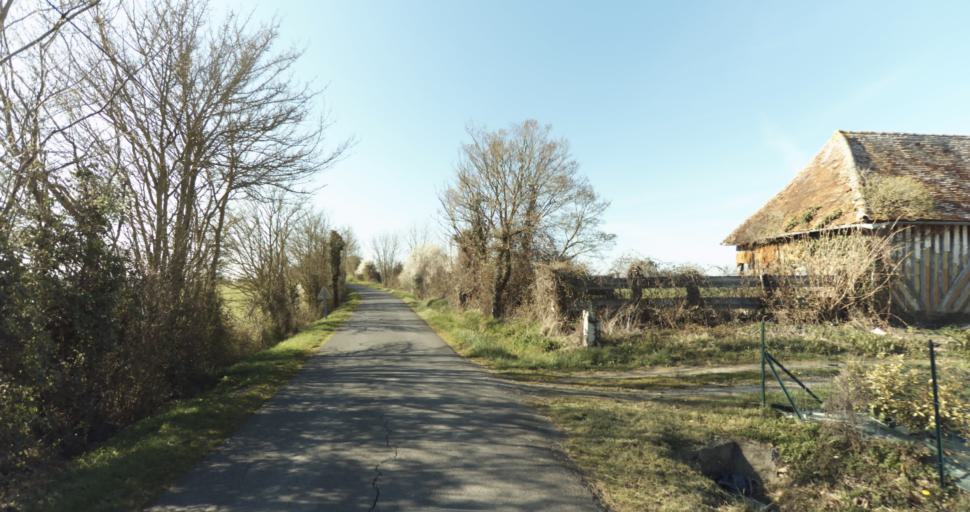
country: FR
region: Lower Normandy
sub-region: Departement du Calvados
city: Saint-Pierre-sur-Dives
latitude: 49.0433
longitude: 0.0386
